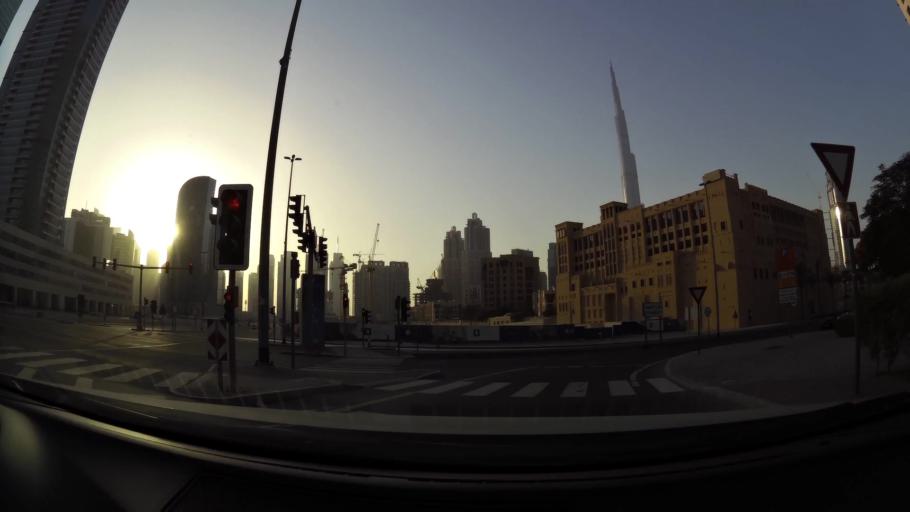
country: AE
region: Dubai
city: Dubai
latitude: 25.1864
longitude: 55.2762
